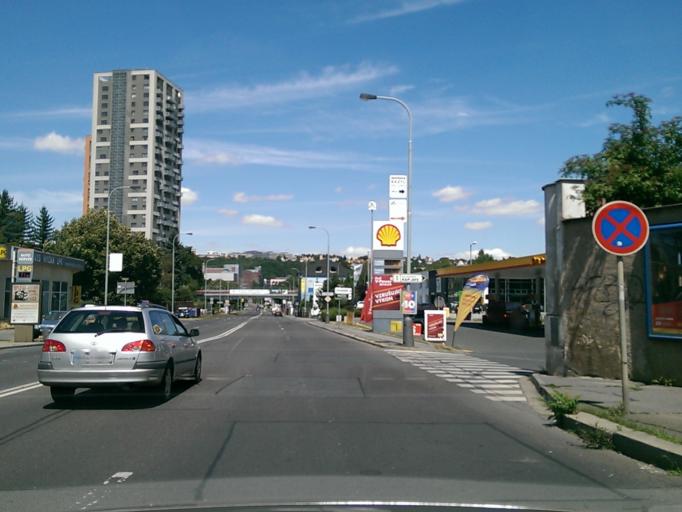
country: CZ
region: Praha
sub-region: Praha 9
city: Prosek
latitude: 50.1032
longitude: 14.5032
